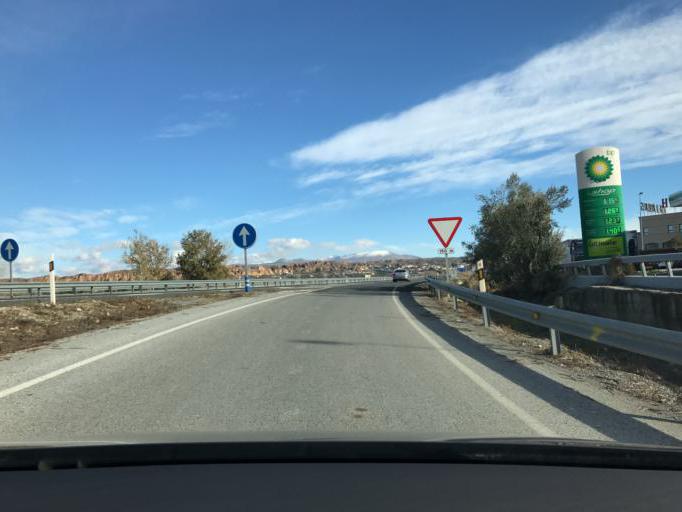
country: ES
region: Andalusia
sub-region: Provincia de Granada
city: Guadix
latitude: 37.3207
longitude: -3.1589
